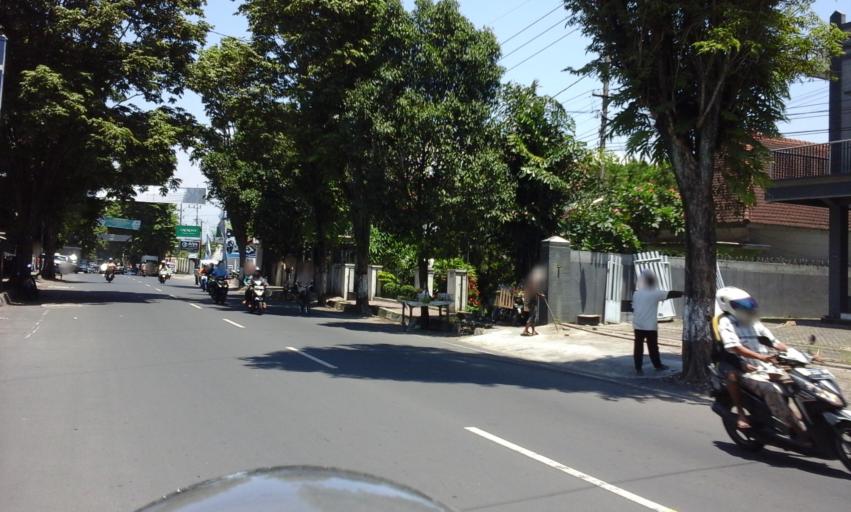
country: ID
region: East Java
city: Sumbersari Wetan
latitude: -8.1816
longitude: 113.7142
